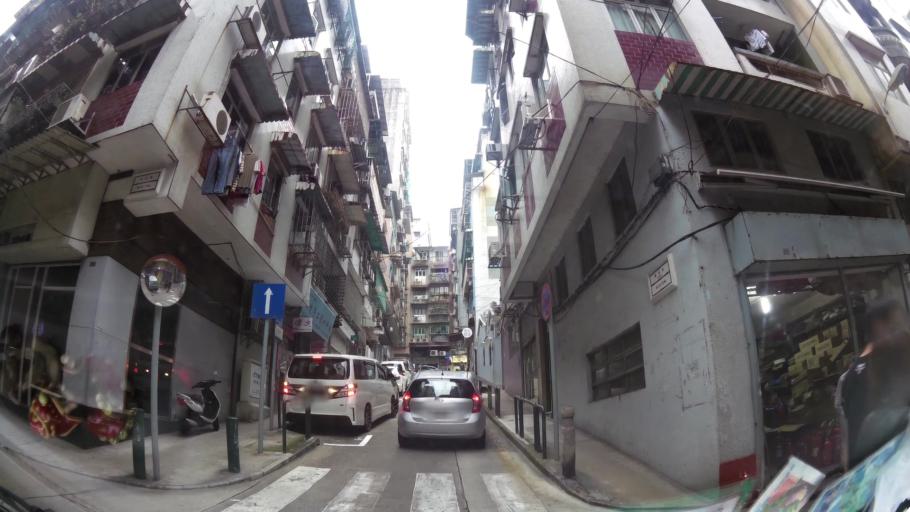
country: MO
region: Macau
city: Macau
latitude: 22.1952
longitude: 113.5457
